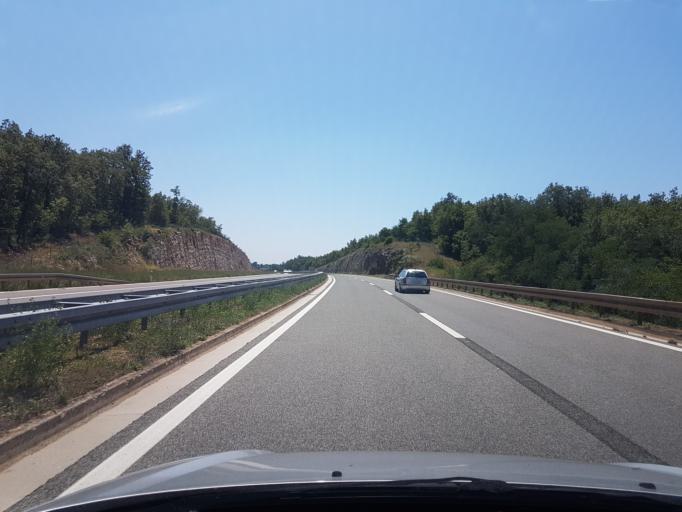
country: HR
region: Istarska
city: Buje
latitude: 45.3888
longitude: 13.6171
